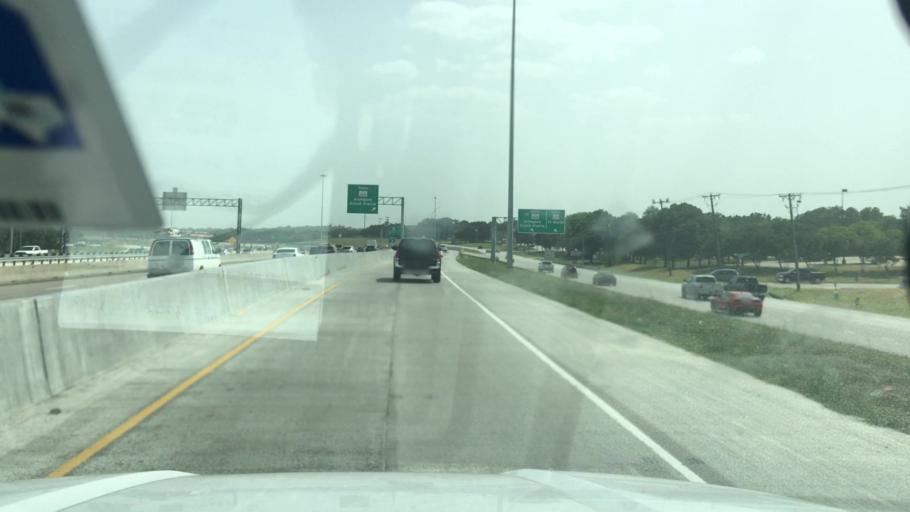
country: US
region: Texas
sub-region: Tarrant County
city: Grapevine
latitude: 32.9159
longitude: -97.0962
